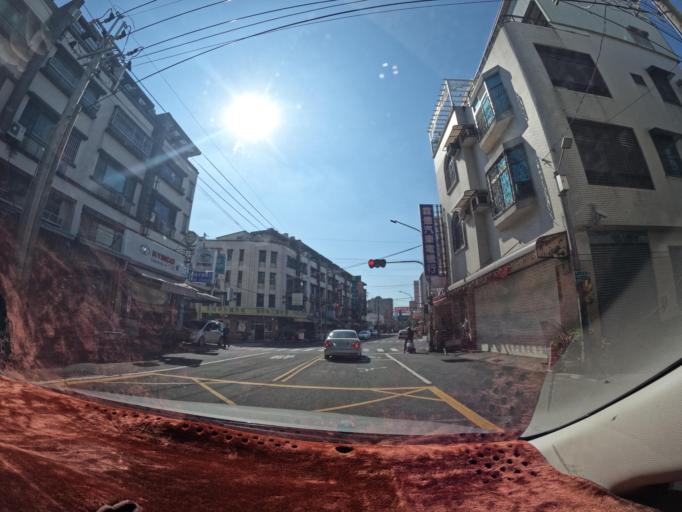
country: TW
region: Taiwan
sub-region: Tainan
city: Tainan
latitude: 23.0187
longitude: 120.2436
